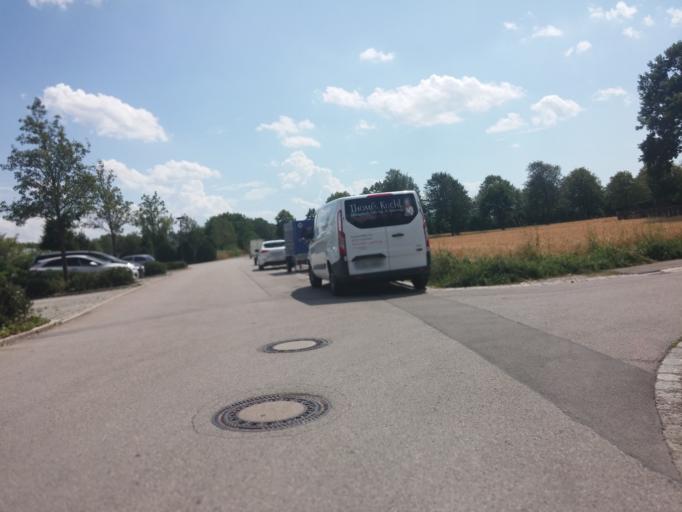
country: DE
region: Bavaria
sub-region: Upper Bavaria
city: Unterhaching
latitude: 48.0816
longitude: 11.6292
